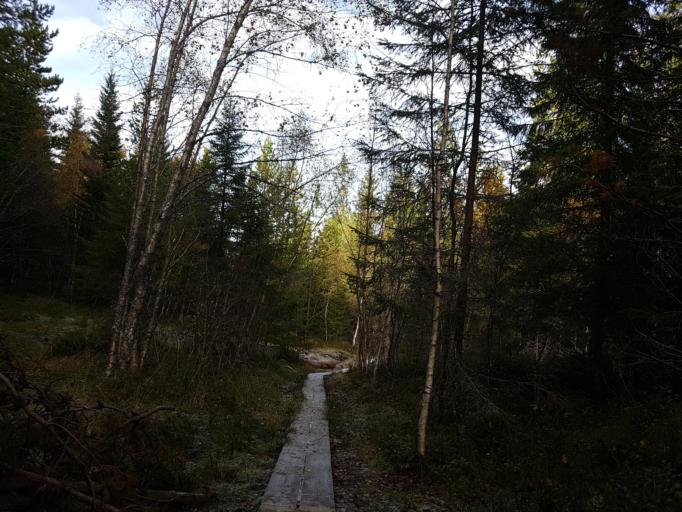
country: NO
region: Sor-Trondelag
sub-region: Trondheim
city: Trondheim
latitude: 63.4463
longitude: 10.2768
